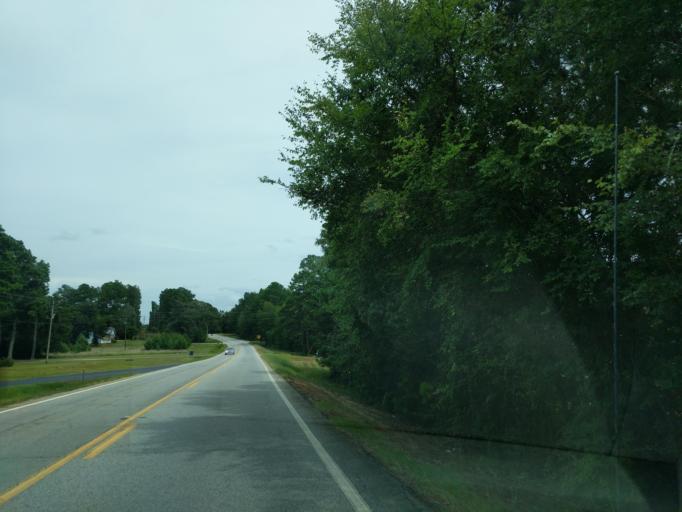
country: US
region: South Carolina
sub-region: Abbeville County
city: Calhoun Falls
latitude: 34.0646
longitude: -82.7310
